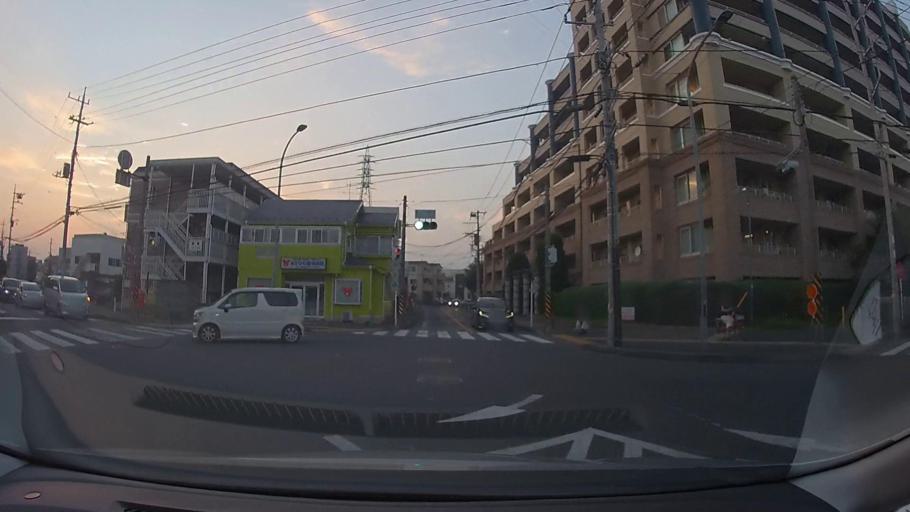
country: JP
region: Kanagawa
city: Minami-rinkan
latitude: 35.5007
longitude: 139.4437
